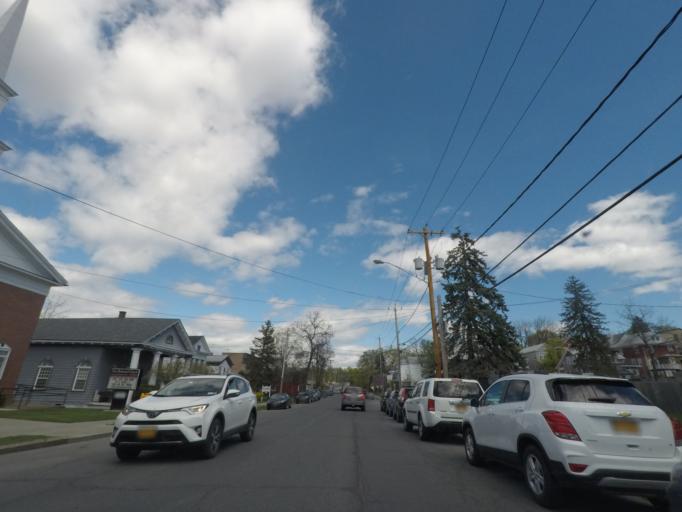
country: US
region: New York
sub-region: Columbia County
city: Oakdale
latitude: 42.2480
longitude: -73.7786
